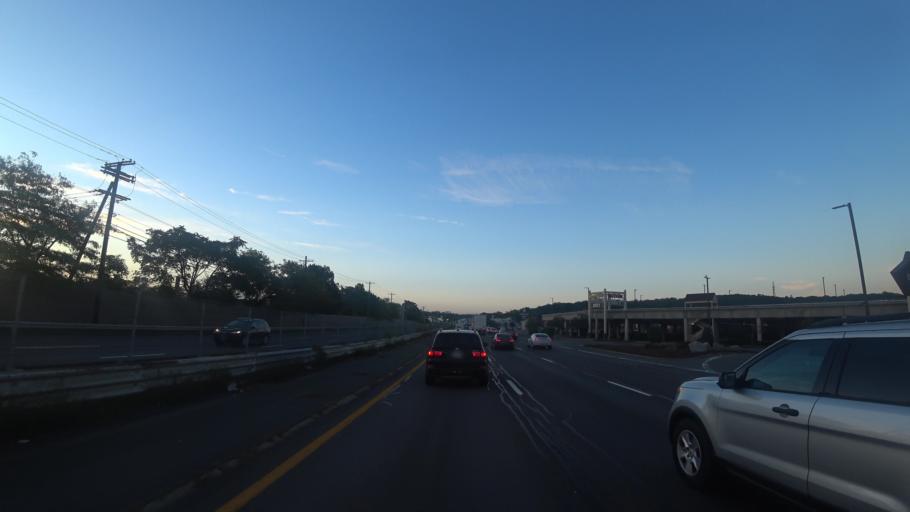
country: US
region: Massachusetts
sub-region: Essex County
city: Saugus
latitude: 42.4629
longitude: -71.0248
